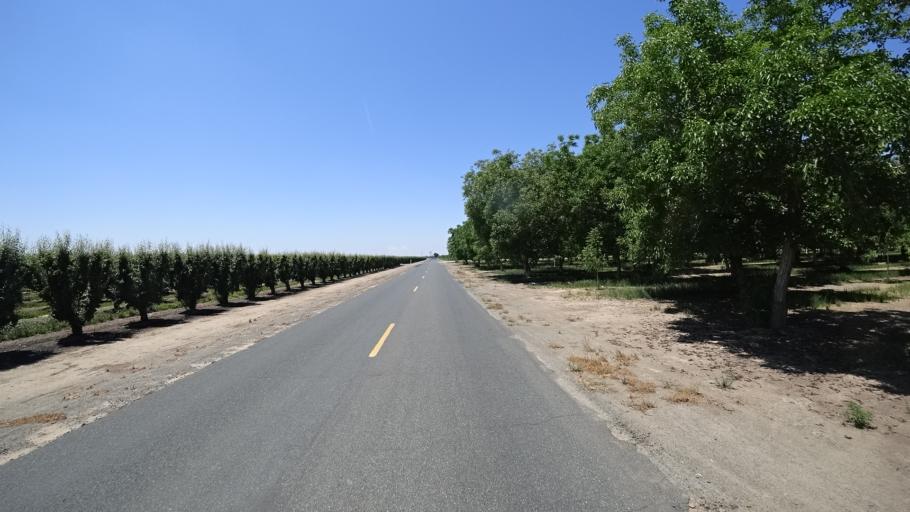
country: US
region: California
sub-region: Fresno County
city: Kingsburg
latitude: 36.4304
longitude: -119.5674
